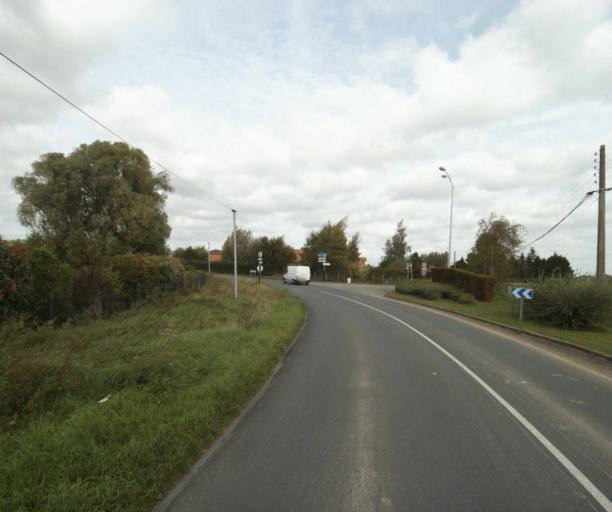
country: FR
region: Nord-Pas-de-Calais
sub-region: Departement du Nord
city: Erquinghem-Lys
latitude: 50.6672
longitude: 2.8455
